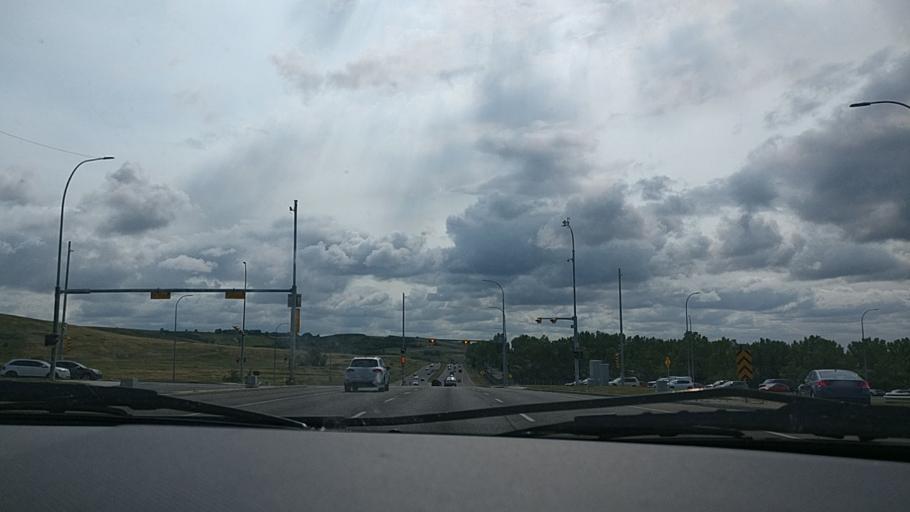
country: CA
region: Alberta
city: Calgary
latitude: 51.1095
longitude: -114.1410
